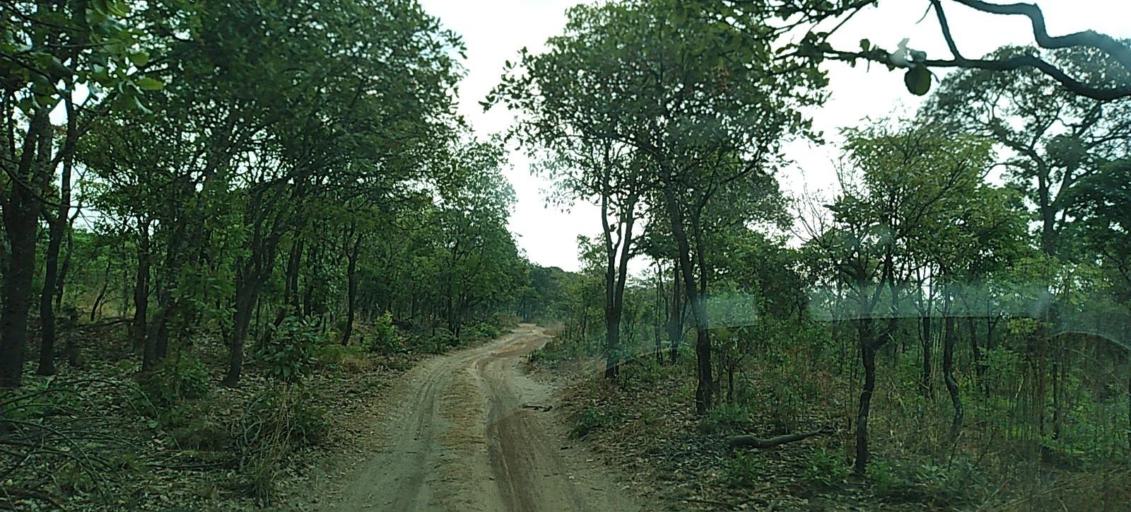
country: ZM
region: North-Western
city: Solwezi
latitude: -12.0974
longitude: 26.2818
